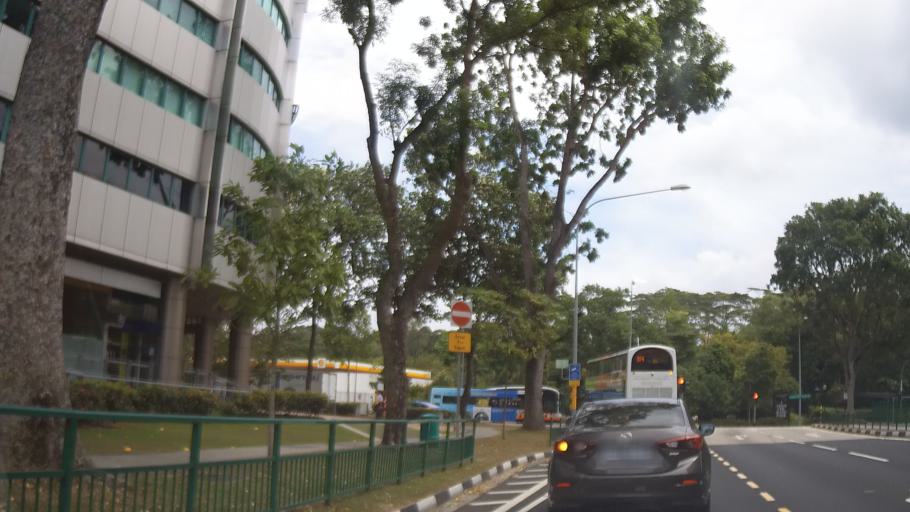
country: MY
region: Johor
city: Johor Bahru
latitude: 1.3848
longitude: 103.7457
